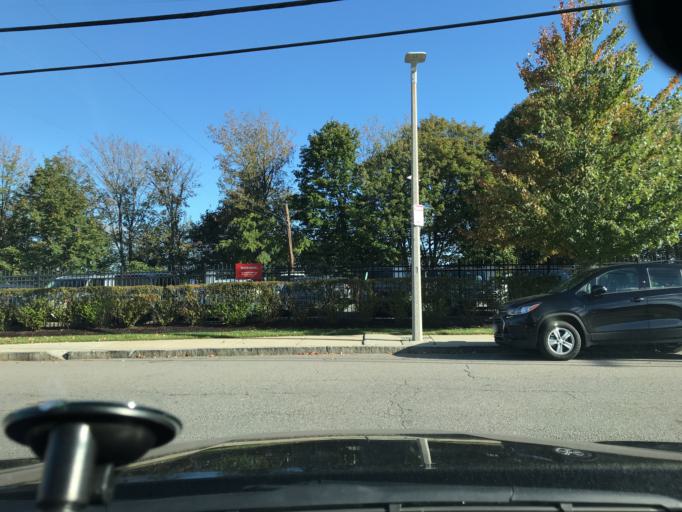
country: US
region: Massachusetts
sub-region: Norfolk County
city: Brookline
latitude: 42.3298
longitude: -71.1059
